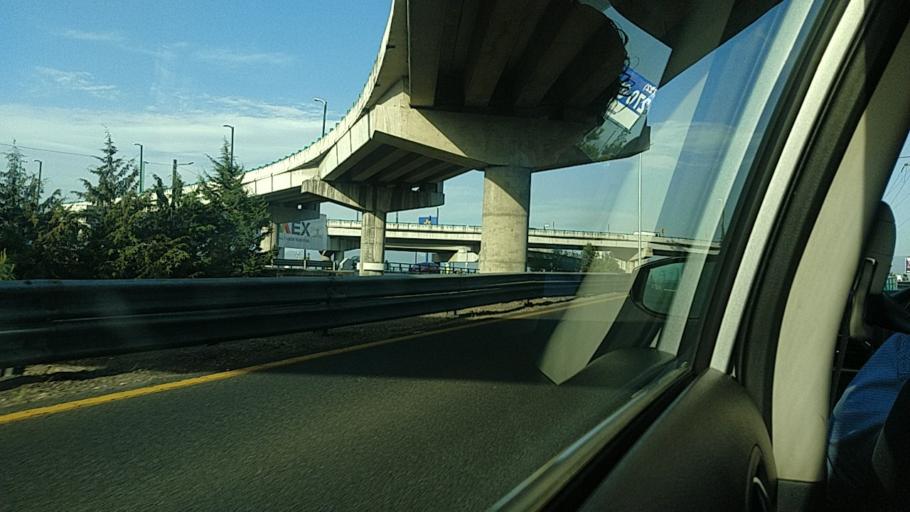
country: MX
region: Mexico
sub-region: San Mateo Atenco
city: Santa Maria la Asuncion
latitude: 19.2860
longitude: -99.5569
